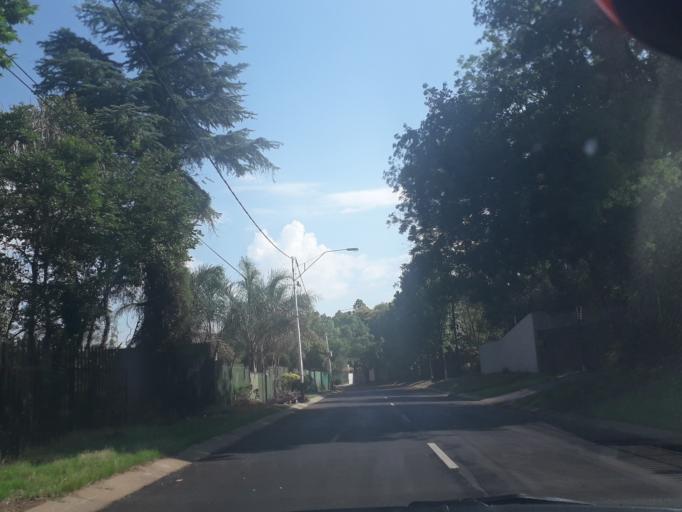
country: ZA
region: Gauteng
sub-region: City of Johannesburg Metropolitan Municipality
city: Modderfontein
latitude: -26.1115
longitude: 28.0742
